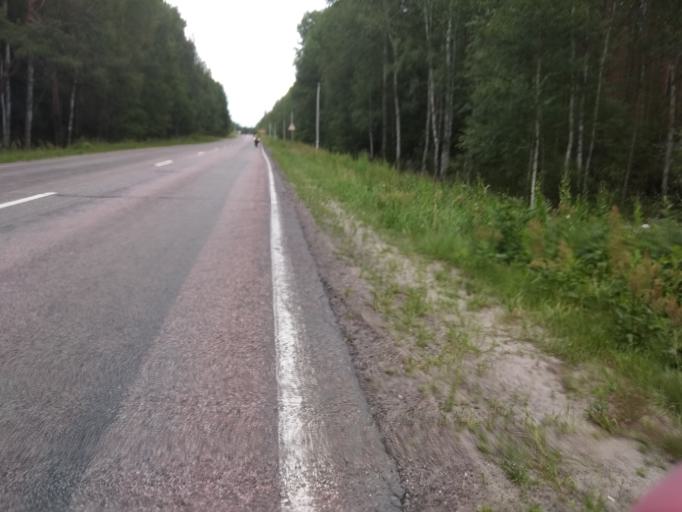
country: RU
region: Moskovskaya
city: Misheronskiy
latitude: 55.6148
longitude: 39.7218
